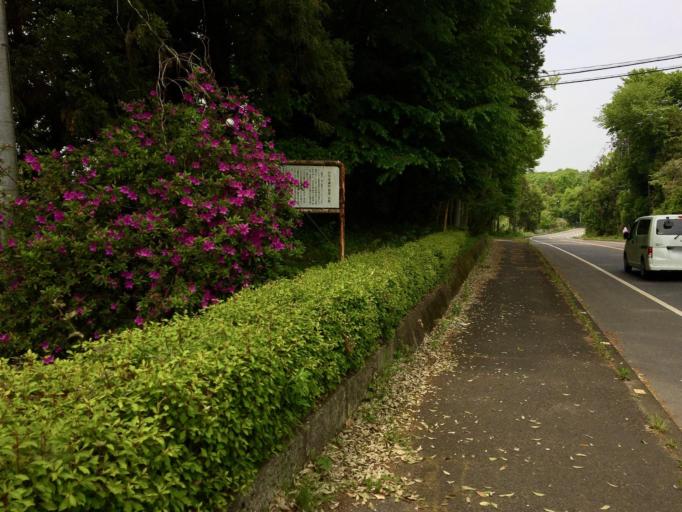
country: JP
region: Tochigi
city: Oyama
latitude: 36.3429
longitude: 139.8153
